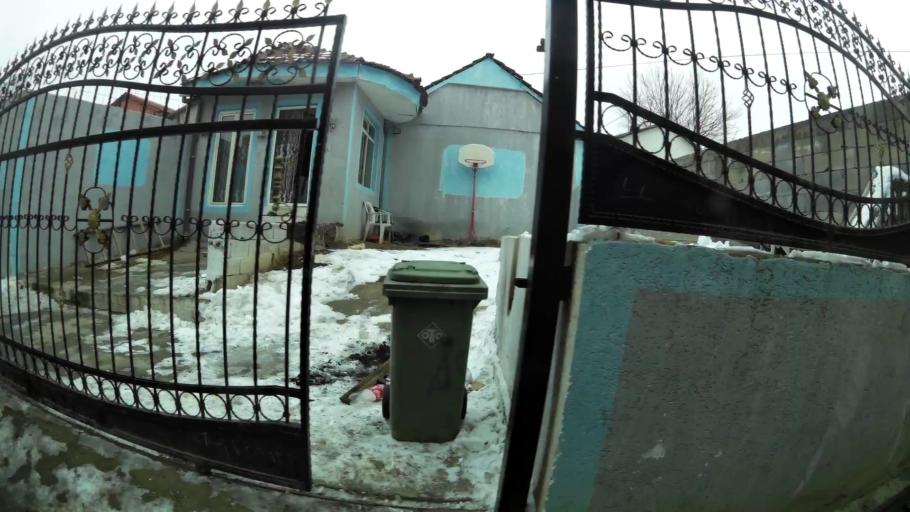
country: MK
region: Suto Orizari
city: Suto Orizare
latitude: 42.0454
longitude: 21.4220
